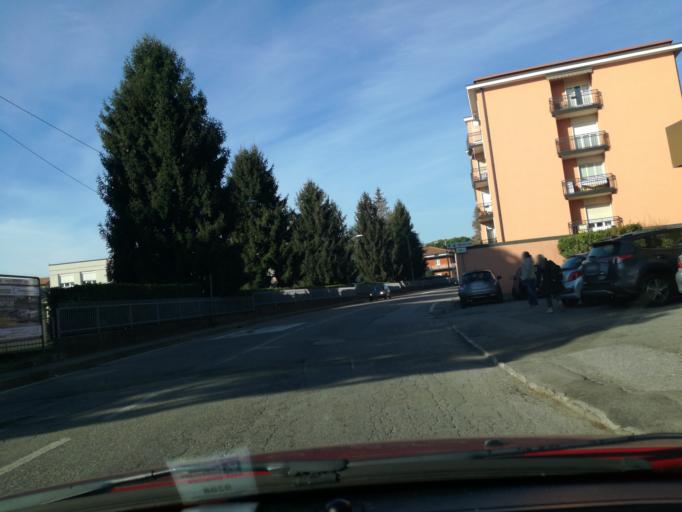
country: IT
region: Lombardy
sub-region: Provincia di Lecco
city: Merate
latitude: 45.6944
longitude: 9.4143
